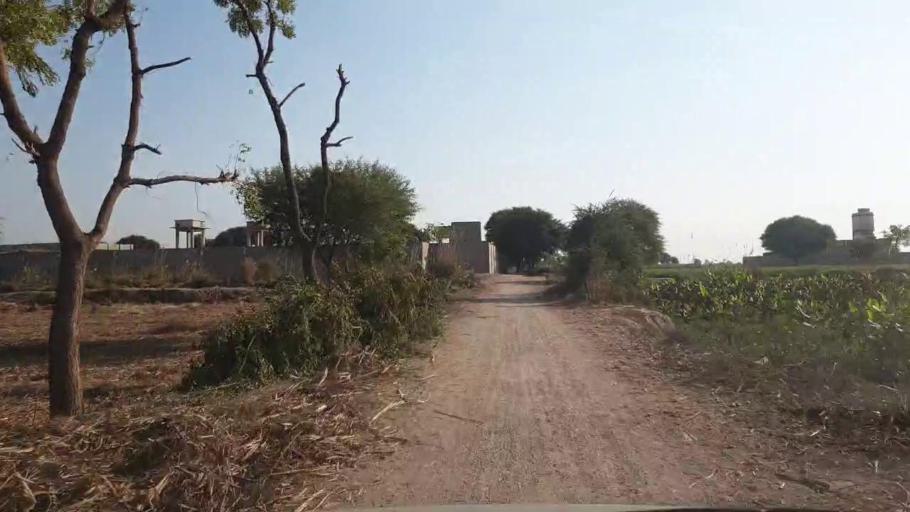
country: PK
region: Sindh
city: Chambar
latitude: 25.3095
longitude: 68.7647
